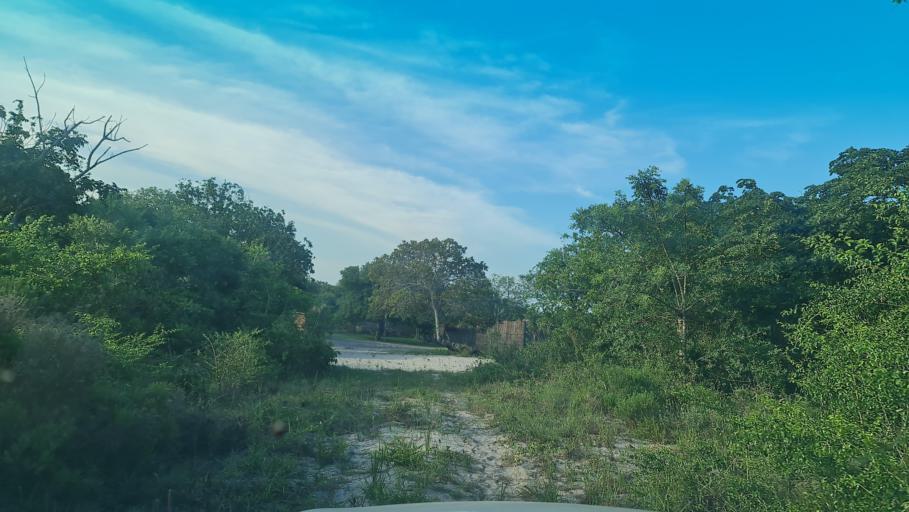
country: MZ
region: Gaza
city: Macia
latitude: -25.2288
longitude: 33.0158
